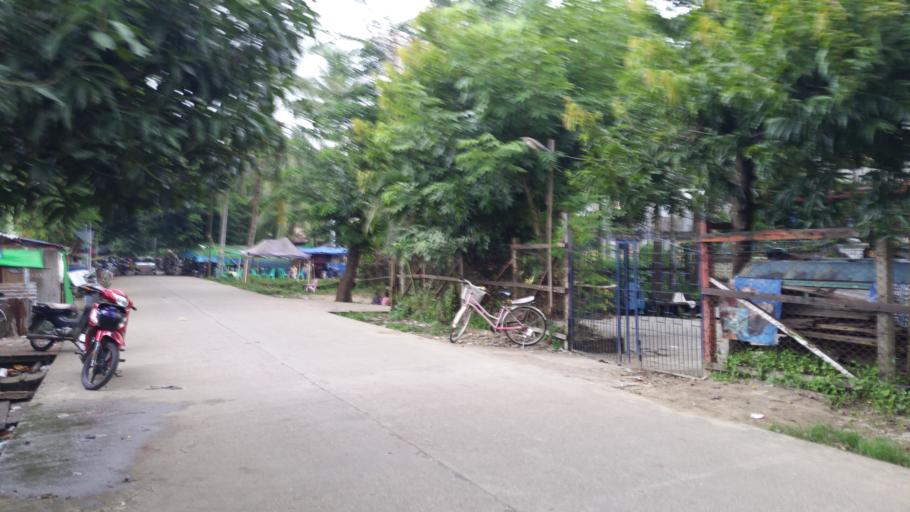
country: MM
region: Yangon
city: Yangon
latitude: 16.7649
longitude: 96.1457
